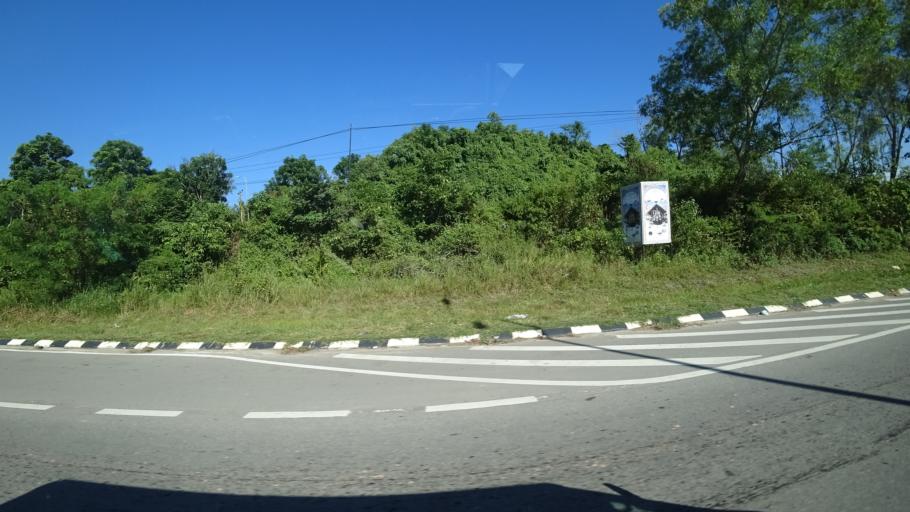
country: MY
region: Sabah
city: Kota Kinabalu
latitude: 6.1439
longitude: 116.2206
